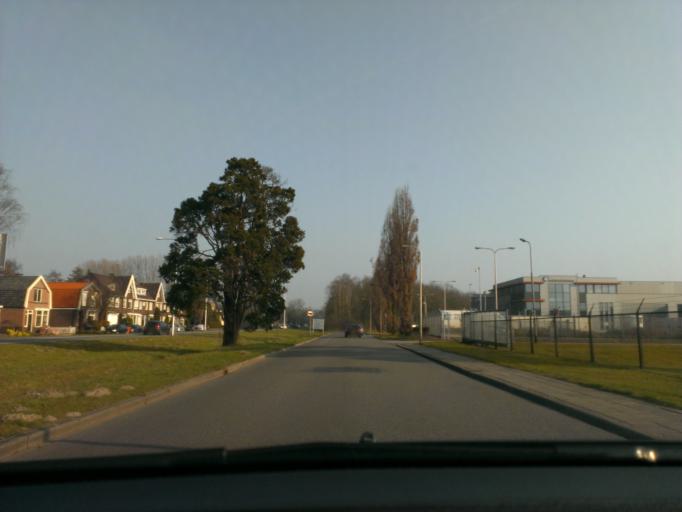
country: NL
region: Overijssel
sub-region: Gemeente Almelo
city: Almelo
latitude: 52.3407
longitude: 6.6910
